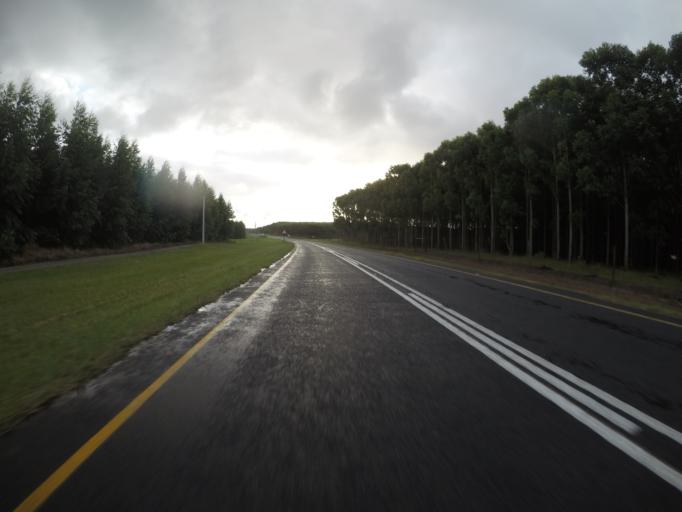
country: ZA
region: KwaZulu-Natal
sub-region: uMkhanyakude District Municipality
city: Mtubatuba
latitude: -28.3672
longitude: 32.2618
